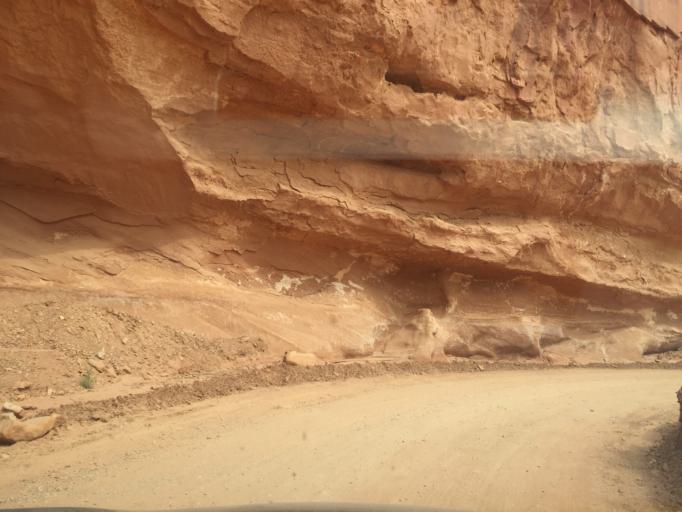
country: US
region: Utah
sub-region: Wayne County
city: Loa
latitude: 38.2644
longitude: -111.2174
